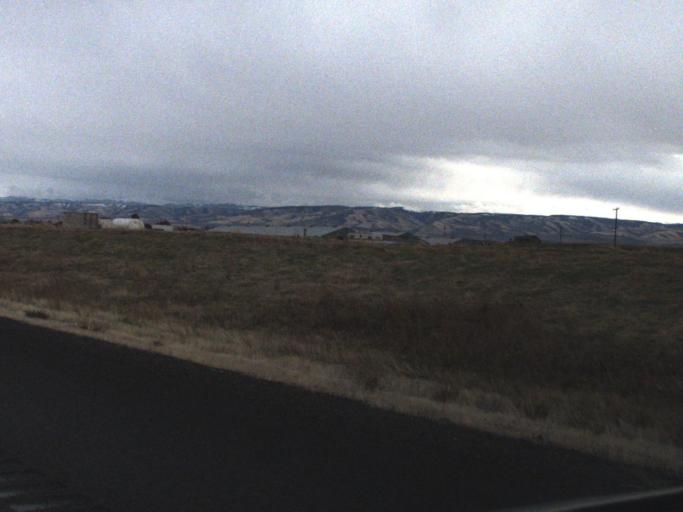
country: US
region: Washington
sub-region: Walla Walla County
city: Garrett
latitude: 46.0498
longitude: -118.4772
